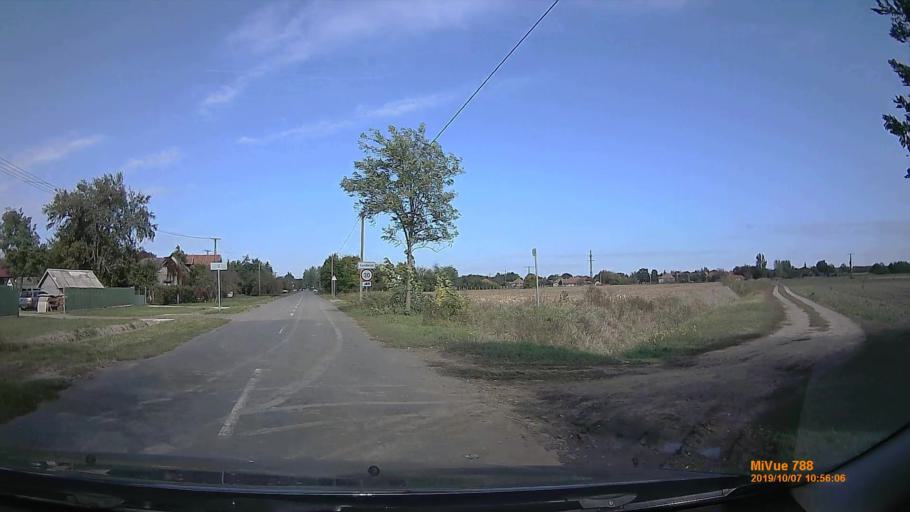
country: HU
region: Bekes
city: Kondoros
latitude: 46.7467
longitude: 20.8029
